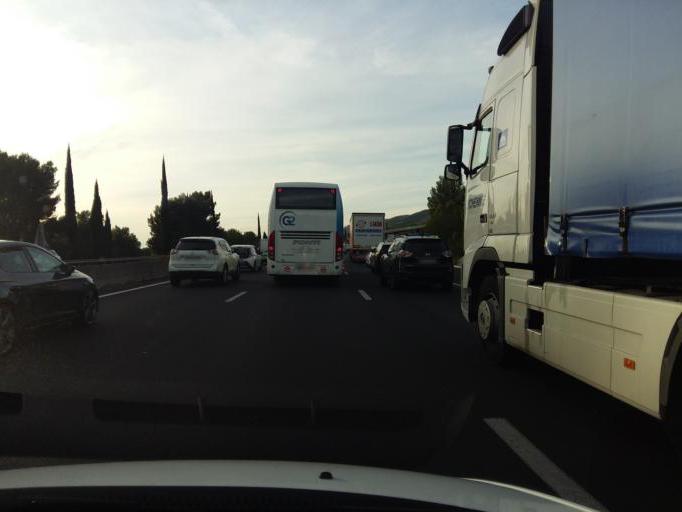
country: FR
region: Provence-Alpes-Cote d'Azur
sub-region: Departement des Bouches-du-Rhone
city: Coudoux
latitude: 43.5519
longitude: 5.2367
